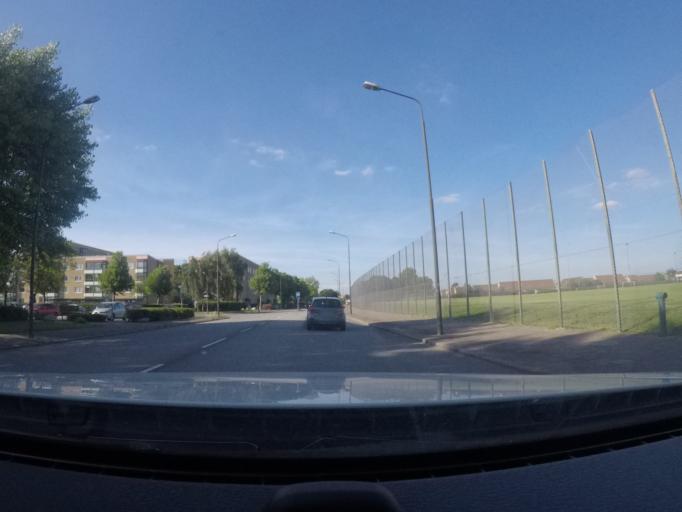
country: SE
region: Skane
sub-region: Malmo
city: Malmoe
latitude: 55.5697
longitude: 13.0224
